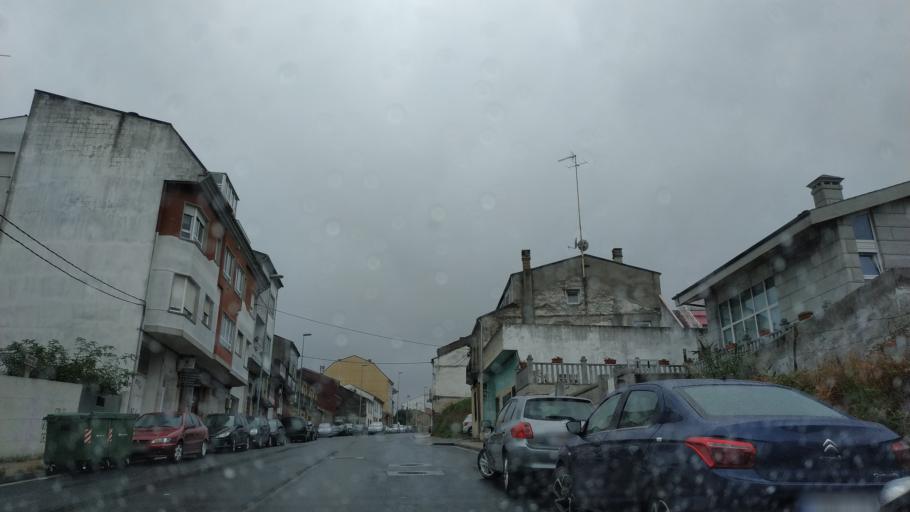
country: ES
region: Galicia
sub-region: Provincia de Lugo
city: Lugo
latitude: 42.9996
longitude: -7.5640
